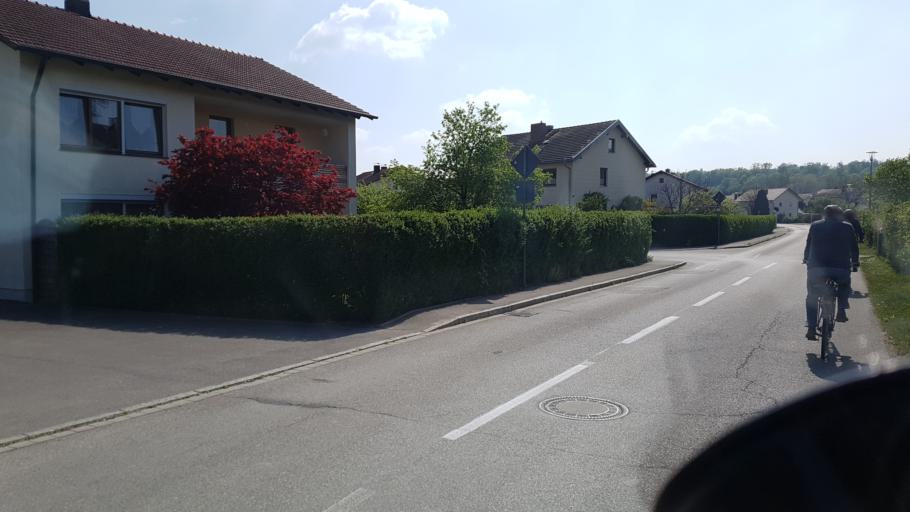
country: DE
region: Bavaria
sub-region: Upper Bavaria
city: Perach
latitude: 48.2435
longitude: 12.7460
